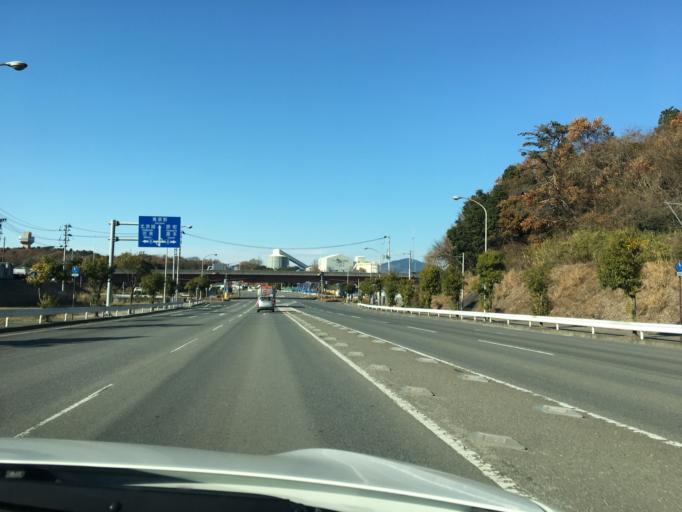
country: JP
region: Fukushima
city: Iwaki
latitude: 36.9364
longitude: 140.8567
